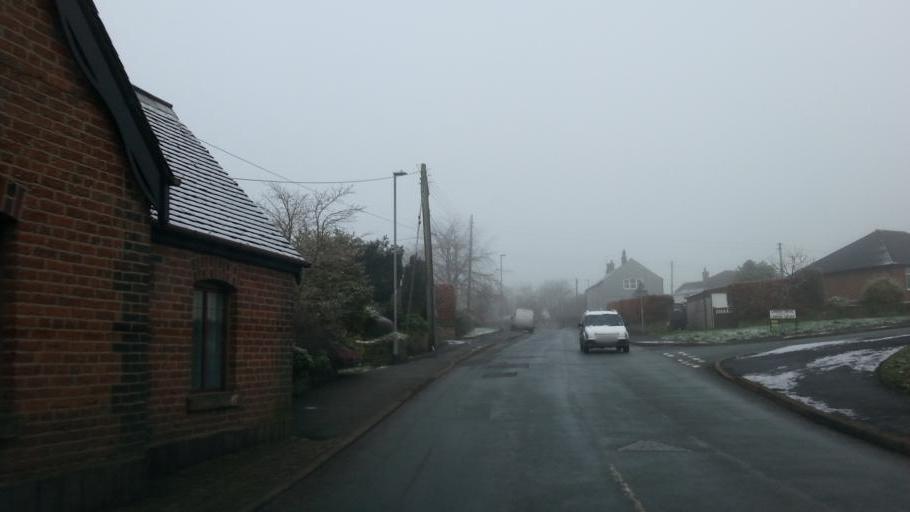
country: GB
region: England
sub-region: Staffordshire
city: Biddulph
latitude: 53.1225
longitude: -2.1788
